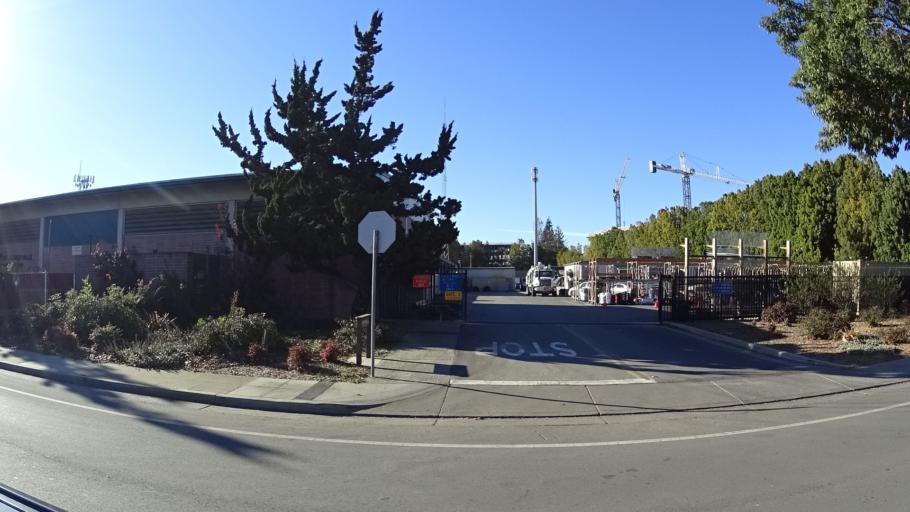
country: US
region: California
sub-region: Santa Clara County
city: Sunnyvale
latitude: 37.3789
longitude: -122.0078
